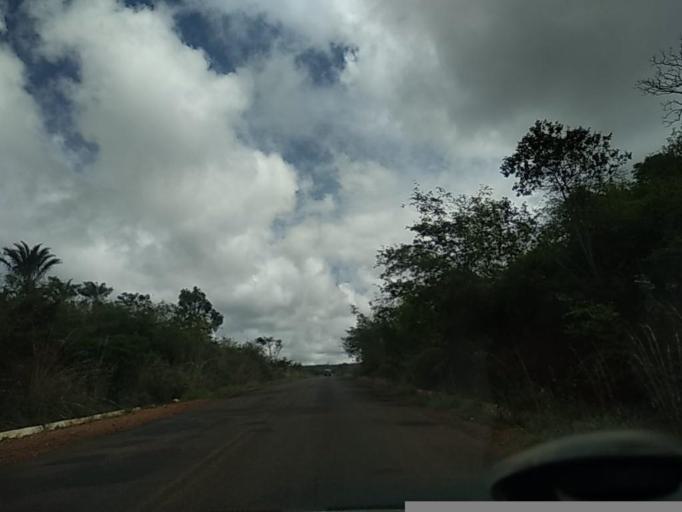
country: BR
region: Bahia
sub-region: Caetite
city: Caetite
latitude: -14.0360
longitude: -42.4867
